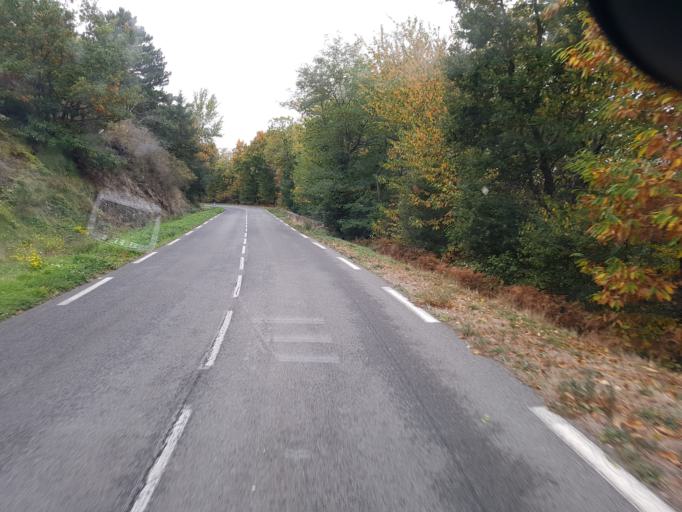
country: FR
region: Languedoc-Roussillon
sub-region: Departement de l'Aude
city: Cuxac-Cabardes
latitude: 43.3719
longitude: 2.3064
